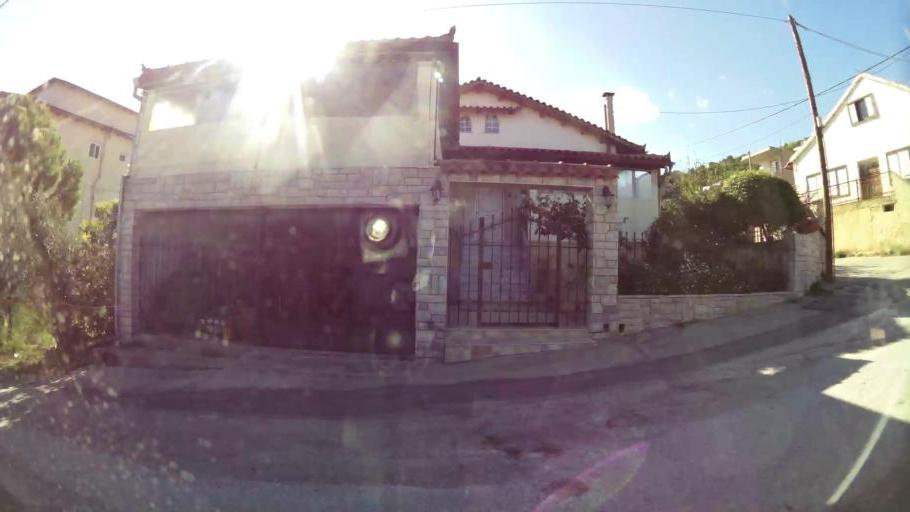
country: GR
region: Attica
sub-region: Nomarchia Anatolikis Attikis
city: Acharnes
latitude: 38.1068
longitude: 23.7195
